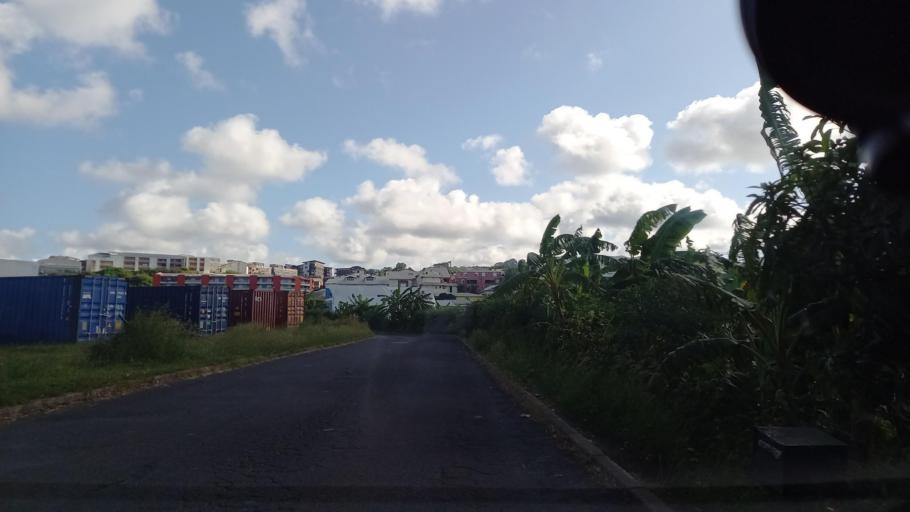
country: YT
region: Mamoudzou
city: Mamoudzou
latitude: -12.7551
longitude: 45.2315
